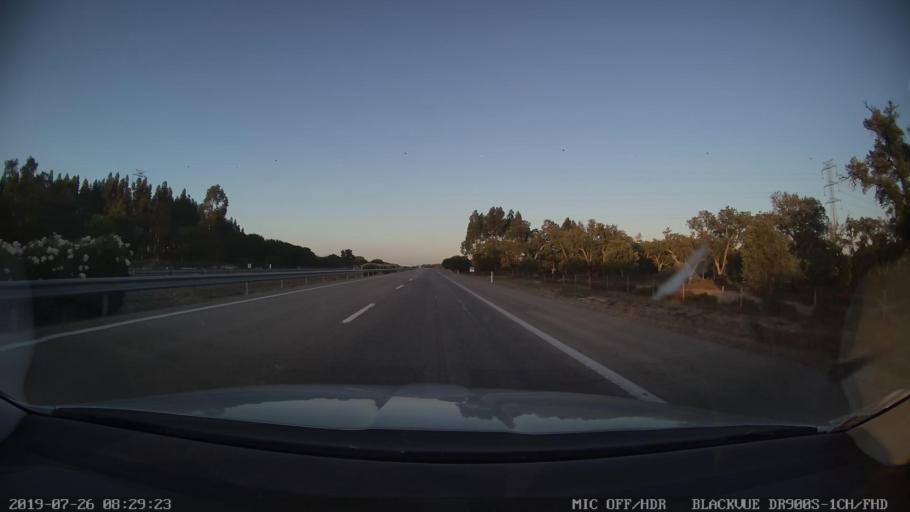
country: PT
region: Evora
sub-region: Vendas Novas
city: Vendas Novas
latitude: 38.6170
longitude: -8.5963
